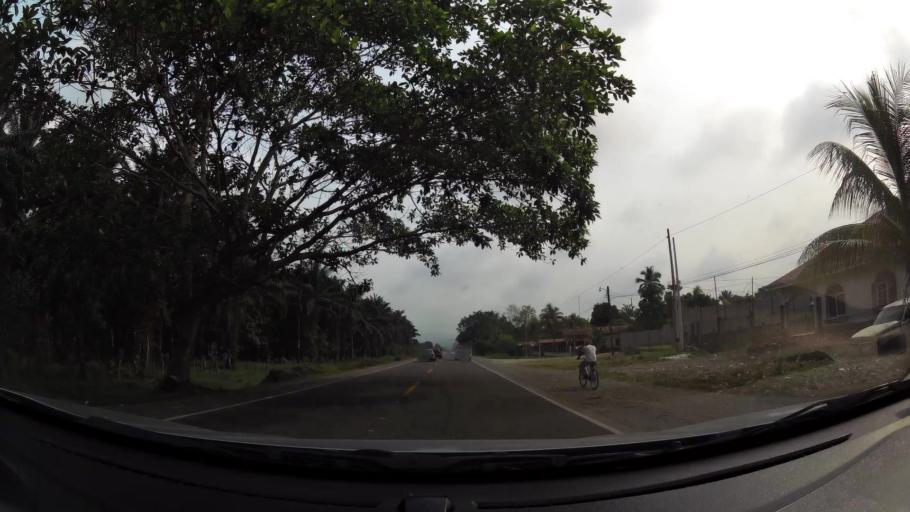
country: HN
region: Yoro
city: Toyos
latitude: 15.5299
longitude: -87.6536
